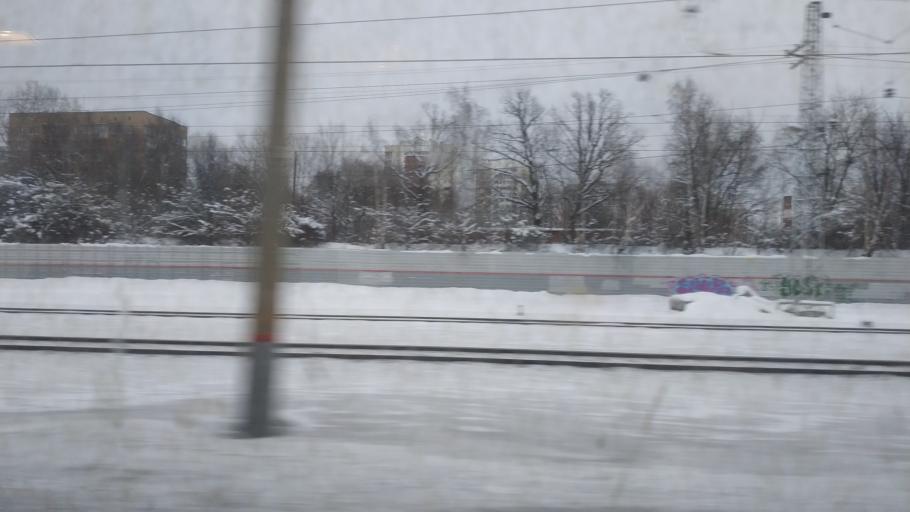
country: RU
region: Moskovskaya
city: Shcherbinka
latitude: 55.5388
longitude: 37.5701
